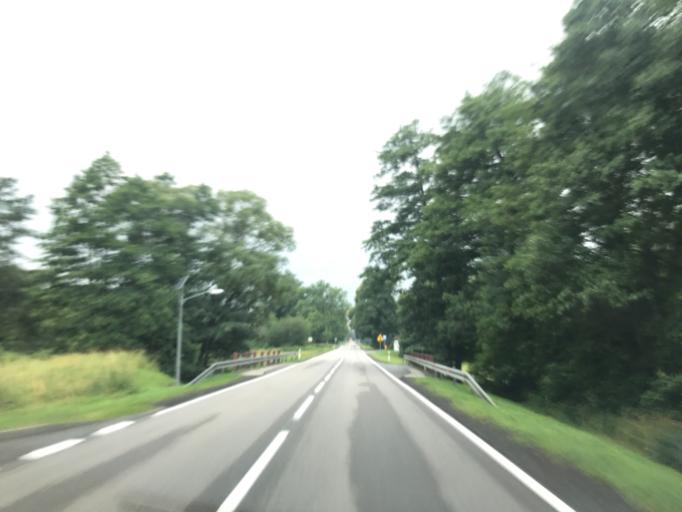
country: PL
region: Pomeranian Voivodeship
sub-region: Powiat czluchowski
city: Rzeczenica
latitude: 53.8035
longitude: 17.0218
